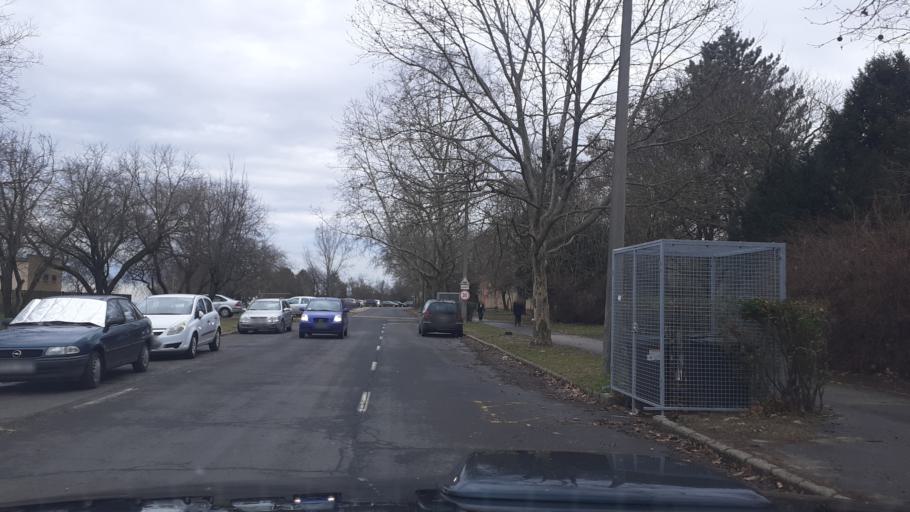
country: HU
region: Fejer
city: dunaujvaros
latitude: 46.9724
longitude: 18.9385
